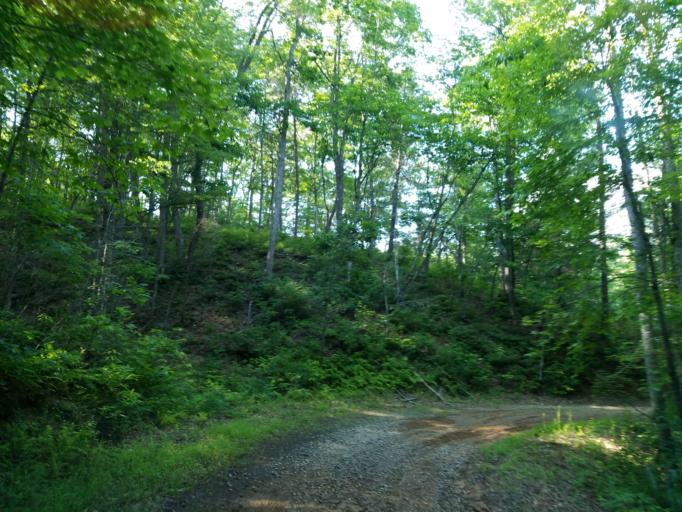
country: US
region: Georgia
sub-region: Fannin County
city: Blue Ridge
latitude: 34.7937
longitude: -84.2010
